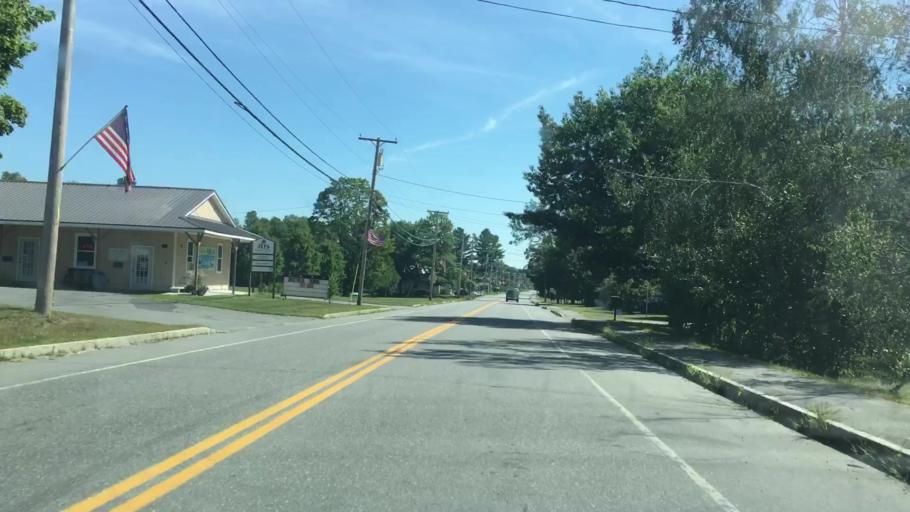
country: US
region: Maine
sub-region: Piscataquis County
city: Milo
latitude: 45.2501
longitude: -68.9818
